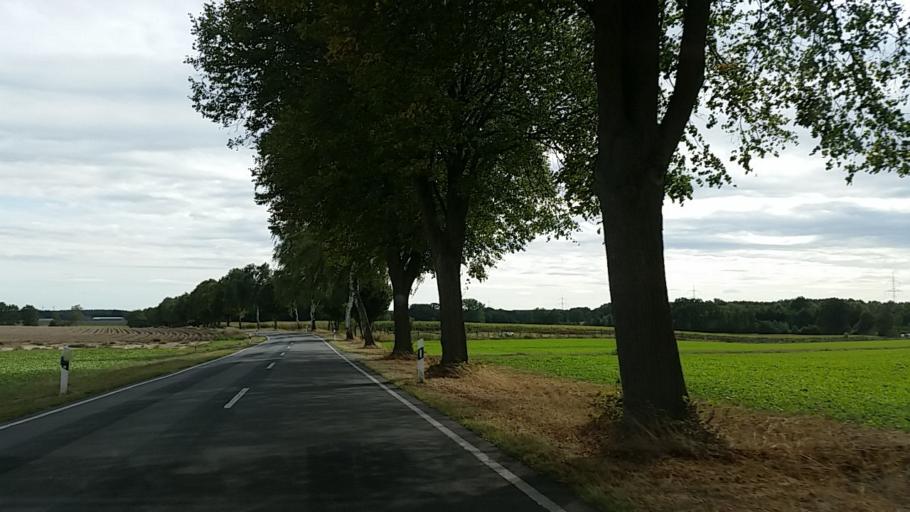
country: DE
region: Lower Saxony
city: Gerdau
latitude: 52.9840
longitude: 10.3927
